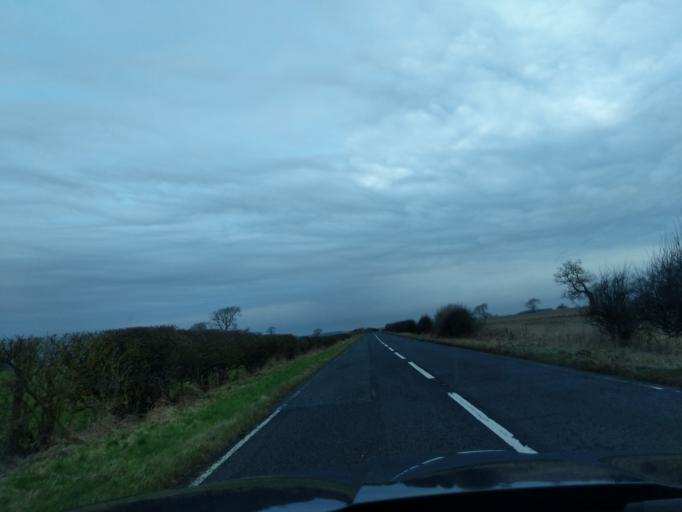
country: GB
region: England
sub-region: Northumberland
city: Rothley
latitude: 55.1322
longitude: -1.9597
